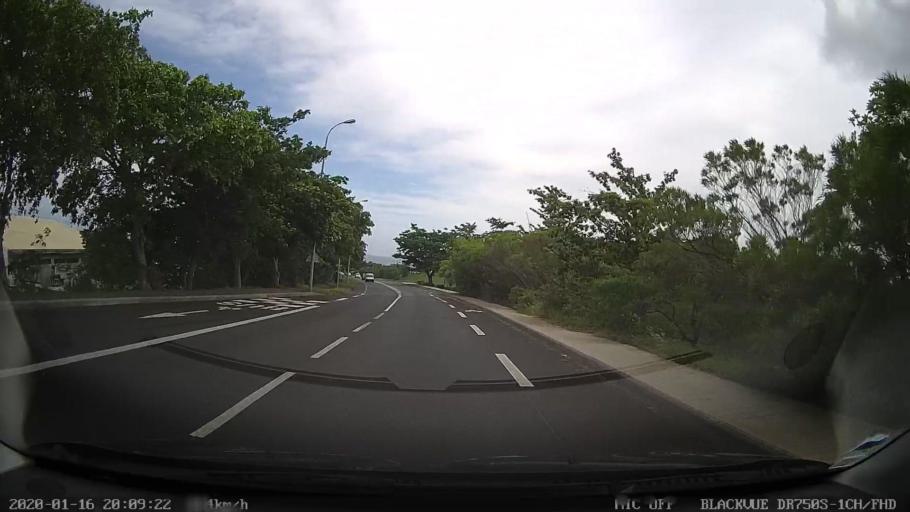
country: RE
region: Reunion
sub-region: Reunion
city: Saint-Denis
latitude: -20.8918
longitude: 55.4715
